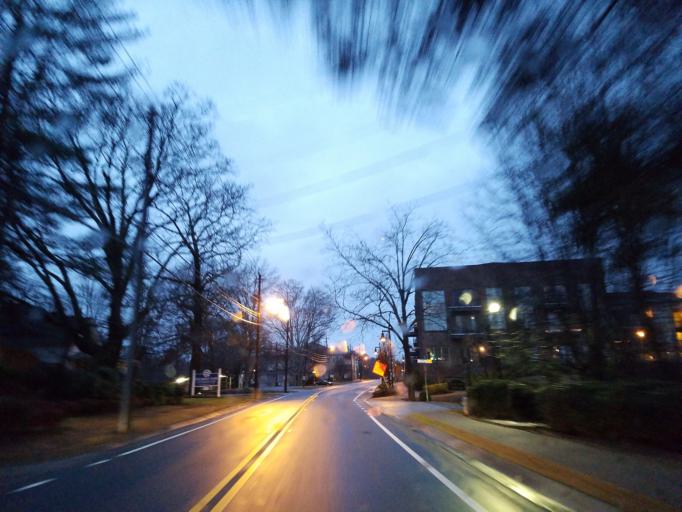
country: US
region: Georgia
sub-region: Fulton County
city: Roswell
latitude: 34.0256
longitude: -84.3544
